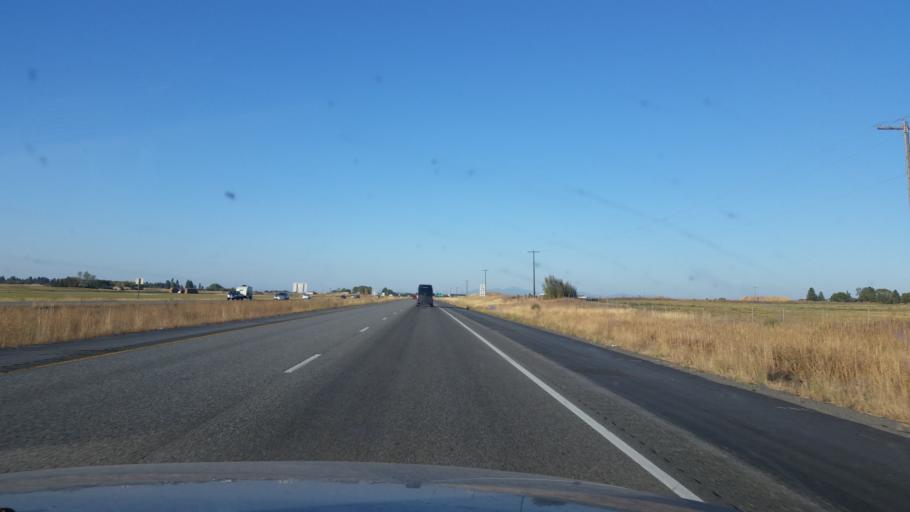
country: US
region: Washington
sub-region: Spokane County
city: Airway Heights
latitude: 47.5719
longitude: -117.5861
